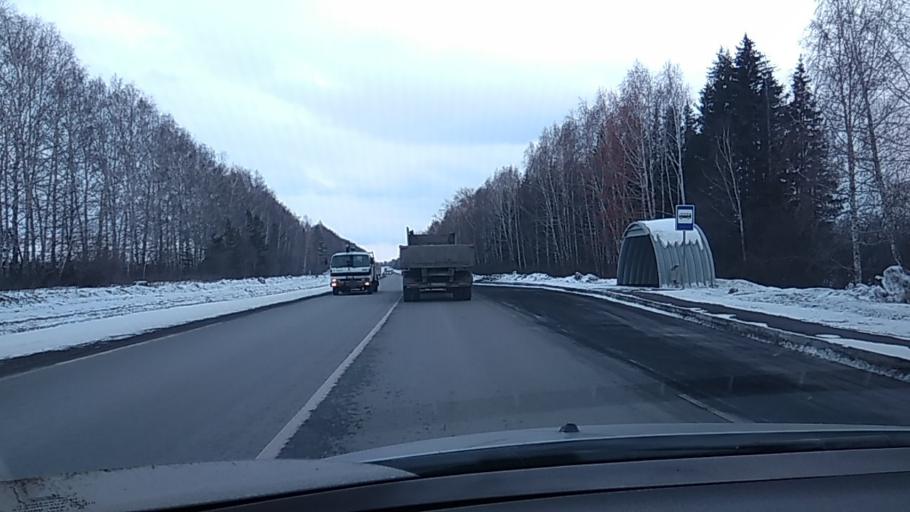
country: RU
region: Sverdlovsk
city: Sovkhoznyy
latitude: 56.5902
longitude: 61.3082
